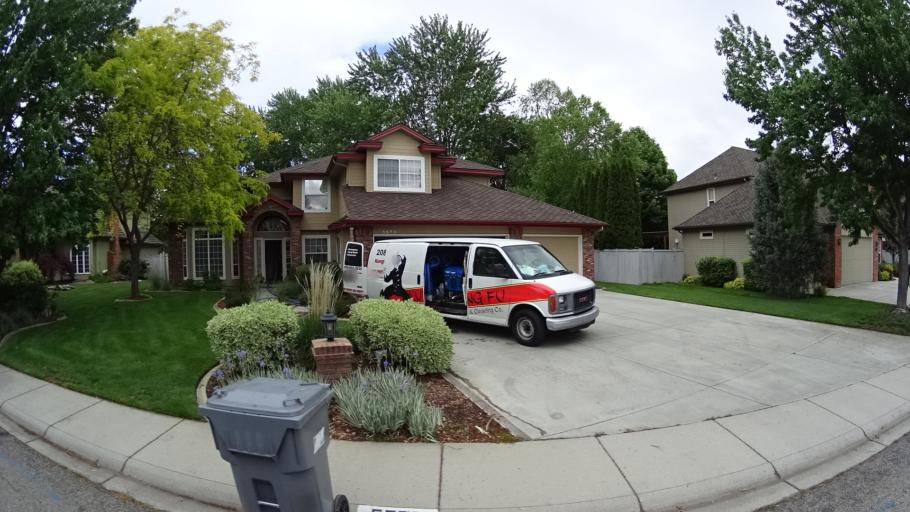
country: US
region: Idaho
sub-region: Ada County
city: Eagle
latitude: 43.6713
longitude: -116.2934
